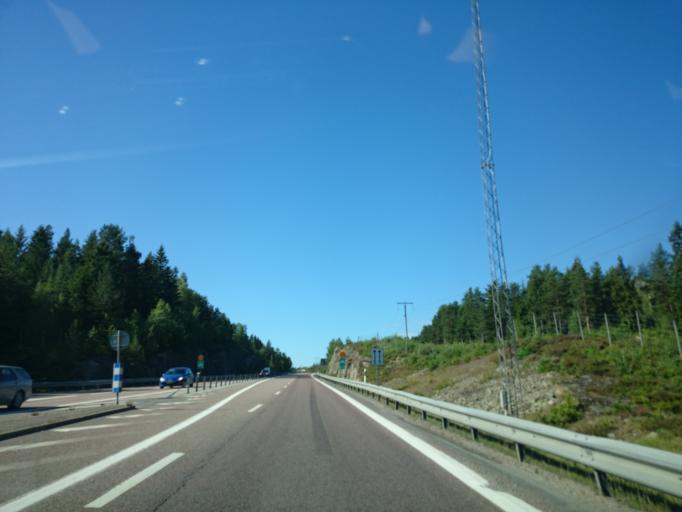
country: SE
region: Gaevleborg
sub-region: Hudiksvalls Kommun
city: Hudiksvall
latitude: 61.7421
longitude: 17.0752
